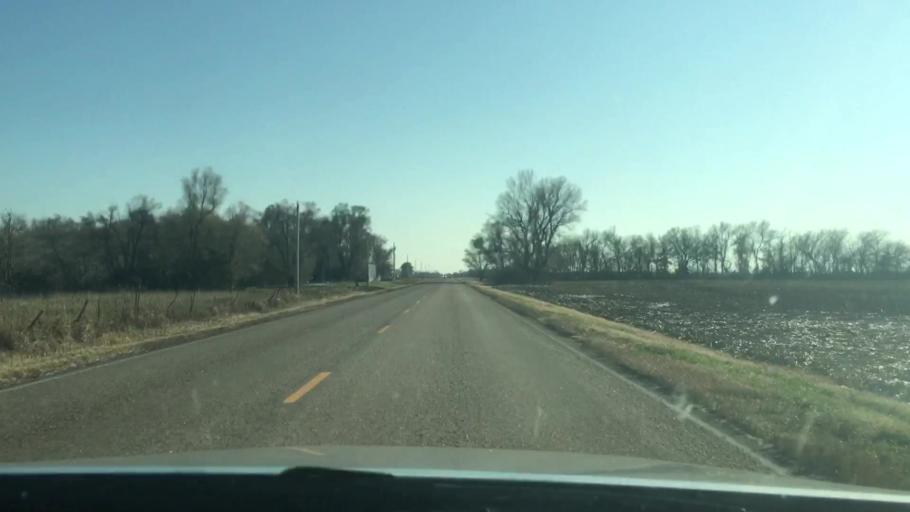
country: US
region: Kansas
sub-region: Reno County
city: Nickerson
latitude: 38.1834
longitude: -98.0876
